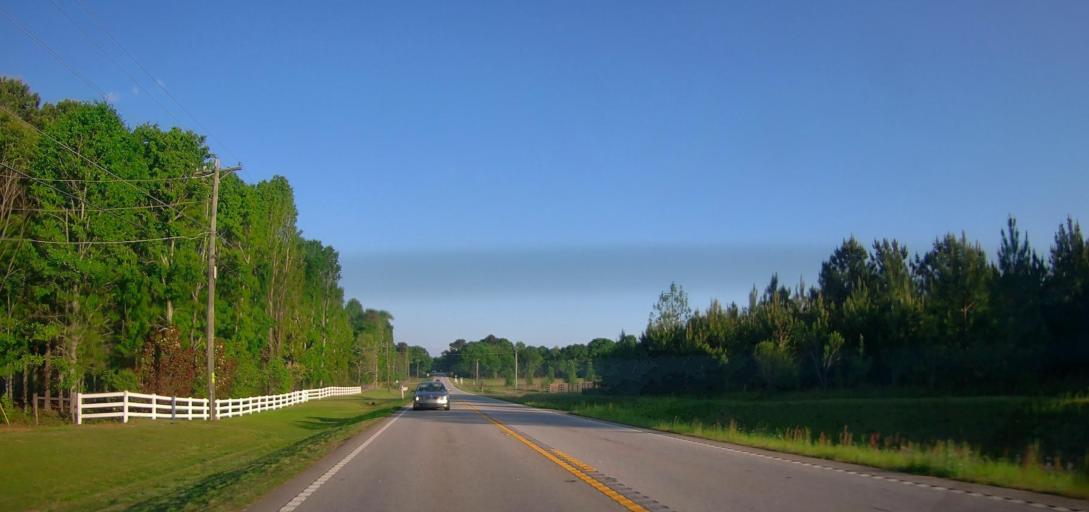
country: US
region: Georgia
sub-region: Walton County
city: Social Circle
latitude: 33.5259
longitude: -83.7049
